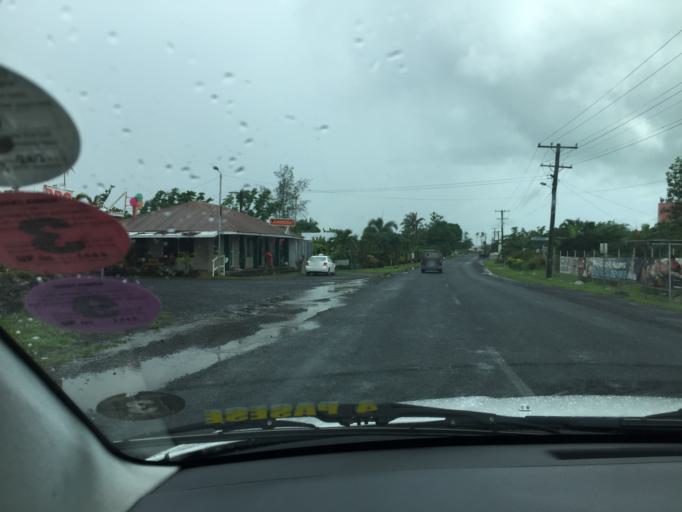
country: WS
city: Faleula
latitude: -13.7960
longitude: -171.8328
